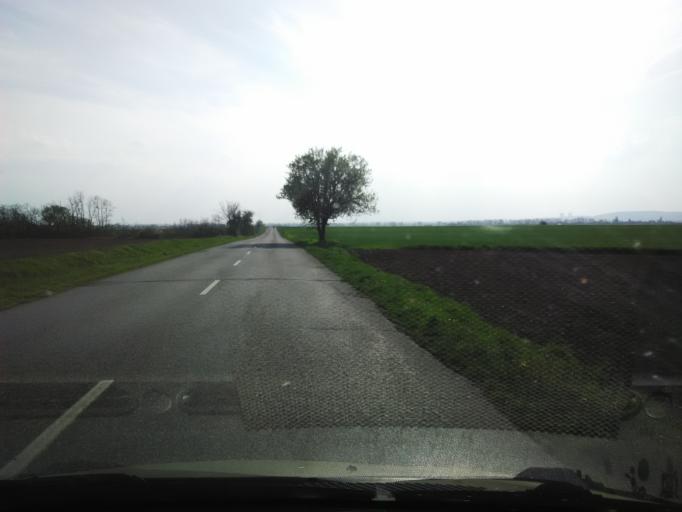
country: SK
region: Nitriansky
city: Levice
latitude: 48.2687
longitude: 18.6218
